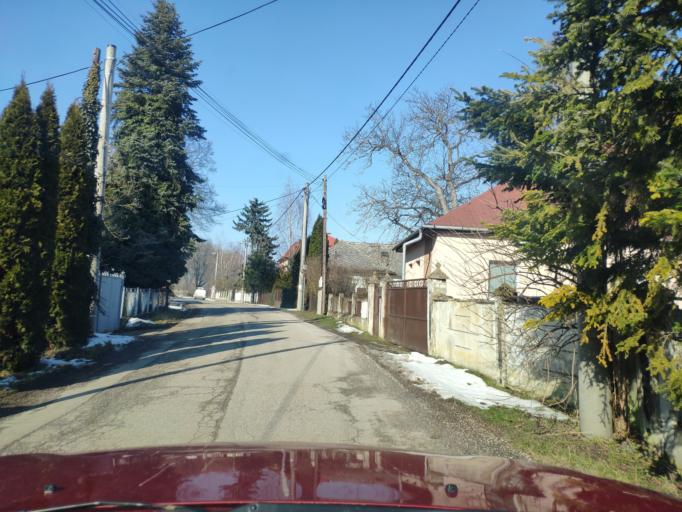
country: HU
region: Borsod-Abauj-Zemplen
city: Gonc
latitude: 48.5830
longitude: 21.2720
